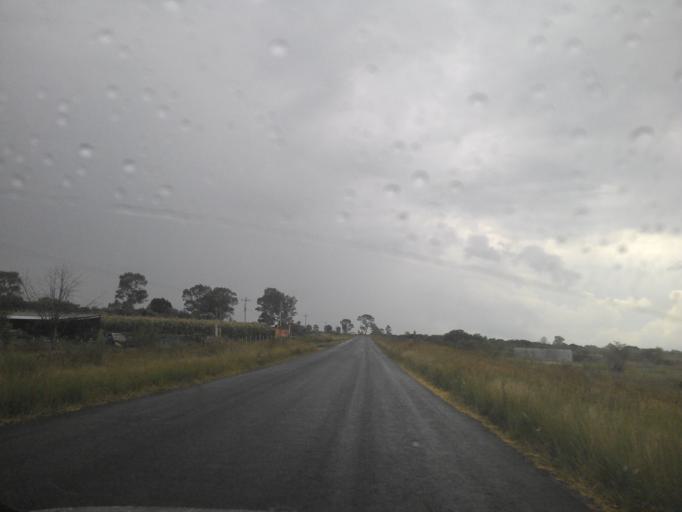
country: MX
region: Jalisco
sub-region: Arandas
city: Santiaguito (Santiaguito de Velazquez)
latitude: 20.8128
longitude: -102.2089
